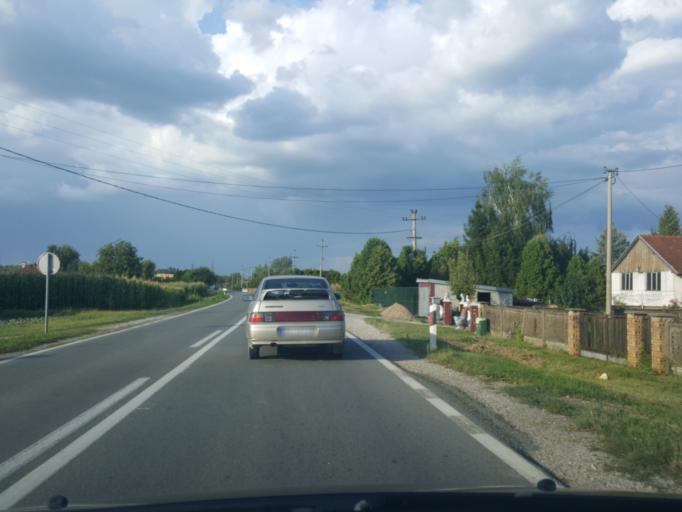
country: RS
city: Lesnica
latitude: 44.6367
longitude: 19.2767
